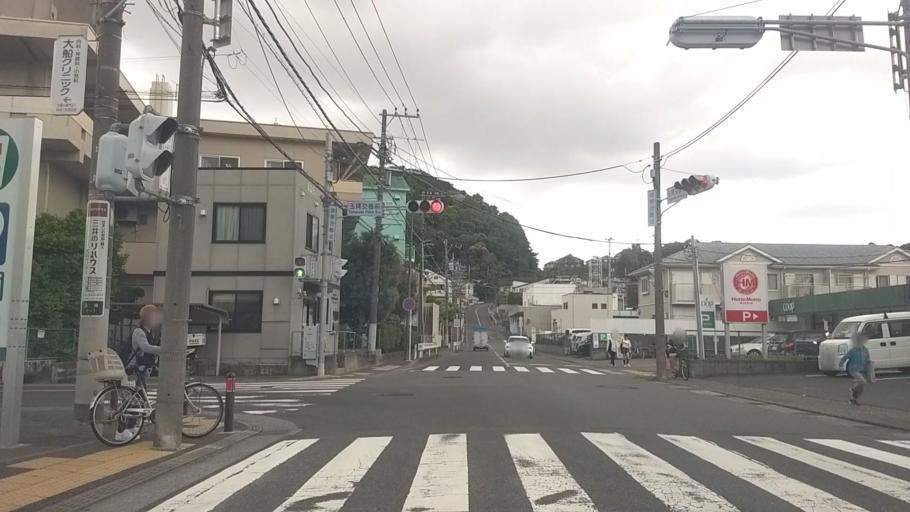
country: JP
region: Kanagawa
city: Kamakura
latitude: 35.3539
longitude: 139.5251
